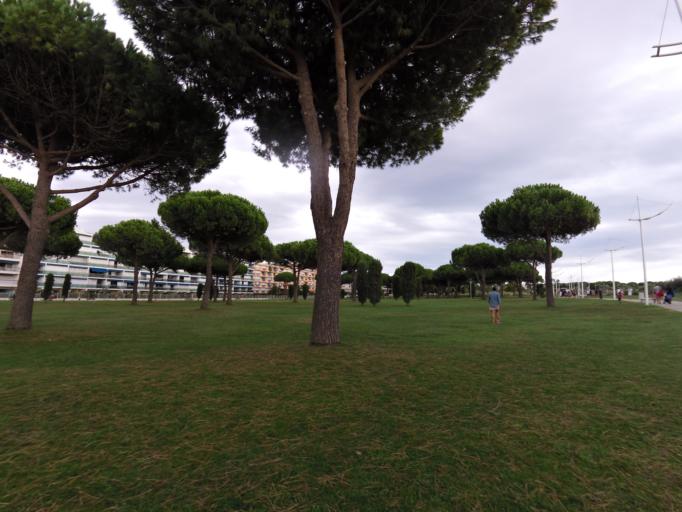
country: FR
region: Languedoc-Roussillon
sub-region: Departement du Gard
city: Le Grau-du-Roi
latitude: 43.5304
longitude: 4.1400
